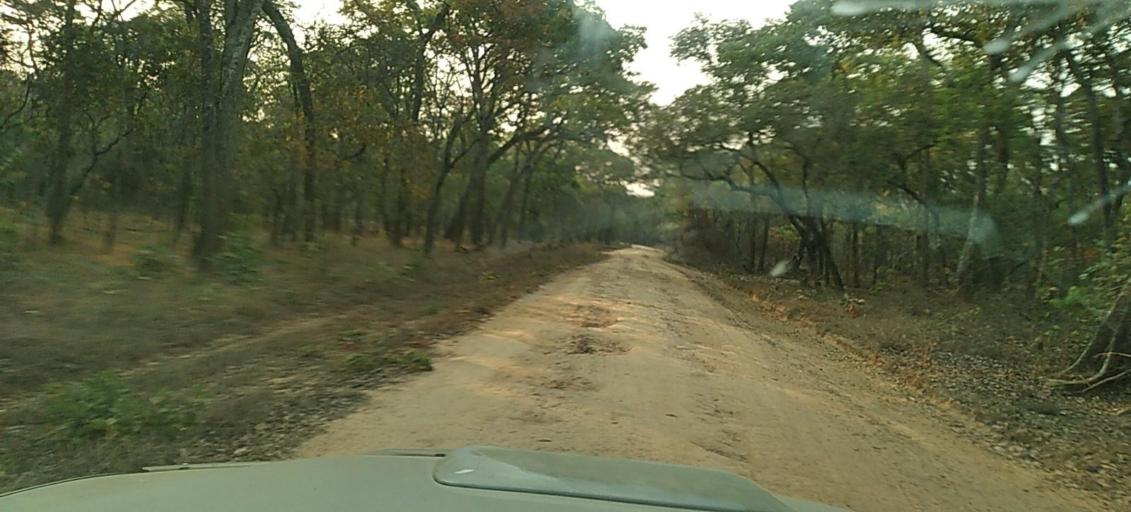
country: ZM
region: North-Western
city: Kasempa
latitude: -13.1595
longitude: 26.4498
